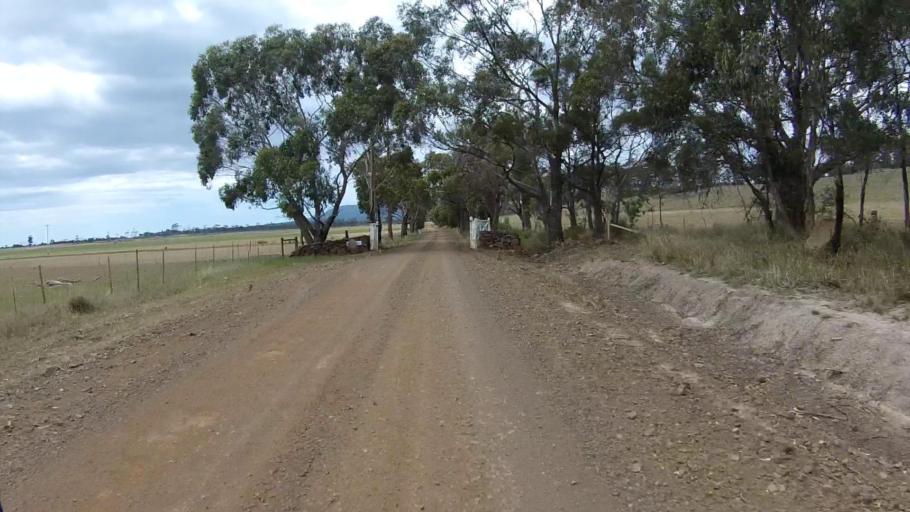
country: AU
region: Tasmania
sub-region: Sorell
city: Sorell
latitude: -42.6545
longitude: 147.9184
